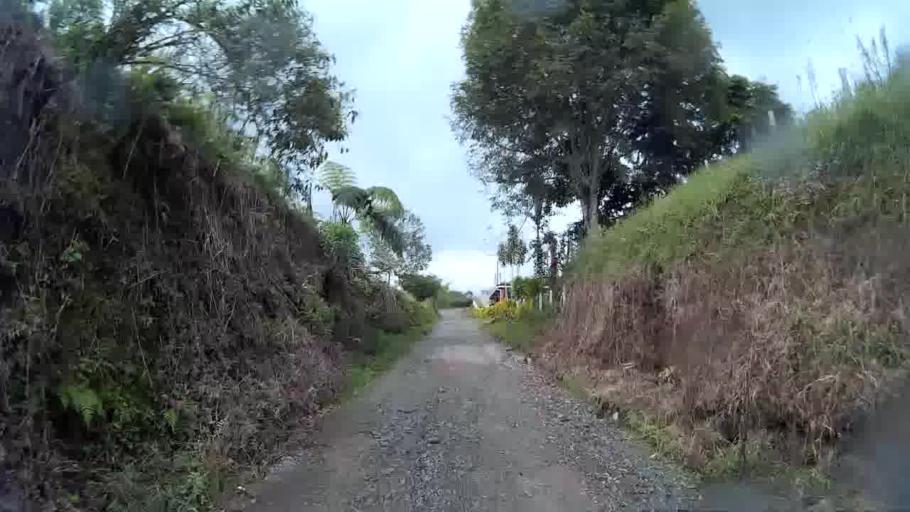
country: CO
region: Quindio
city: Filandia
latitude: 4.6954
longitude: -75.6701
